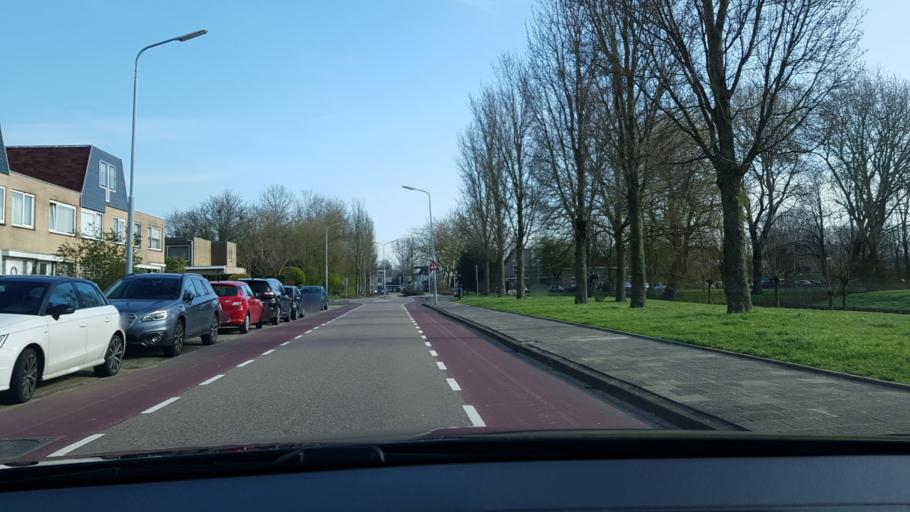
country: NL
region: North Holland
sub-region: Gemeente Haarlemmermeer
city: Hoofddorp
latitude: 52.3059
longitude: 4.7015
